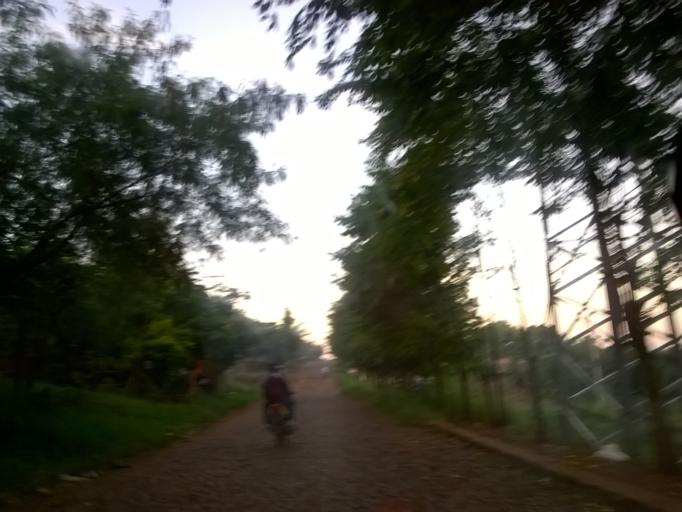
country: PY
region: Alto Parana
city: Ciudad del Este
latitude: -25.4813
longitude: -54.6445
